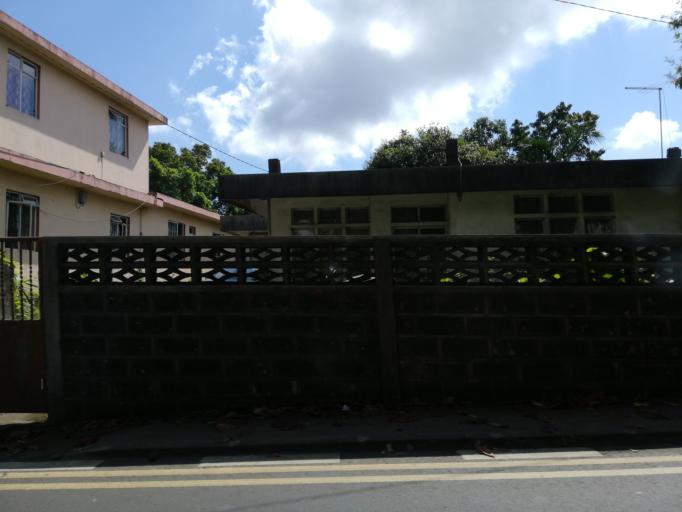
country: MU
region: Moka
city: Verdun
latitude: -20.2234
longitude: 57.5403
